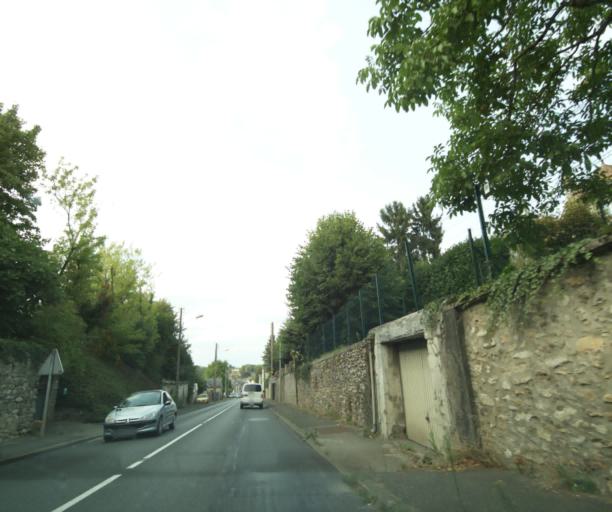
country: FR
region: Centre
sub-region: Departement d'Indre-et-Loire
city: Cormery
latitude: 47.2646
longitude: 0.8358
